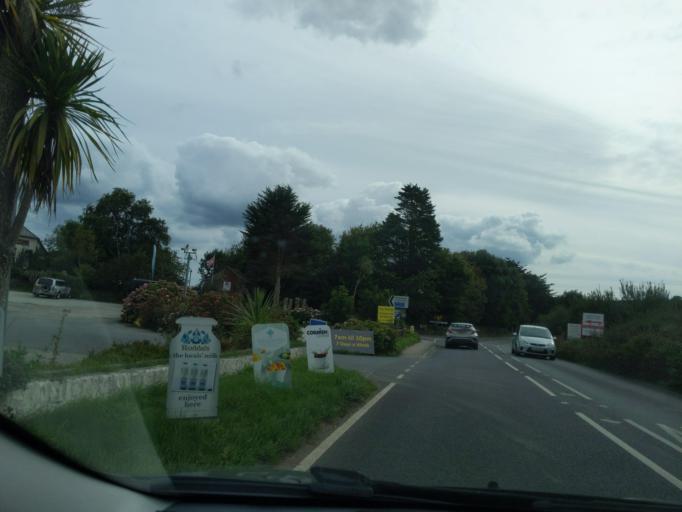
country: GB
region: England
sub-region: Cornwall
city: Mevagissey
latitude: 50.2923
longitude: -4.7862
